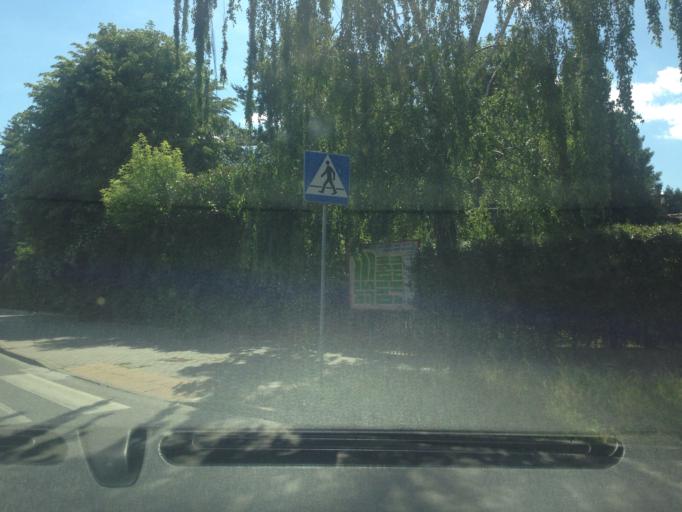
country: PL
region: Masovian Voivodeship
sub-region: Warszawa
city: Bemowo
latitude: 52.2519
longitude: 20.8812
